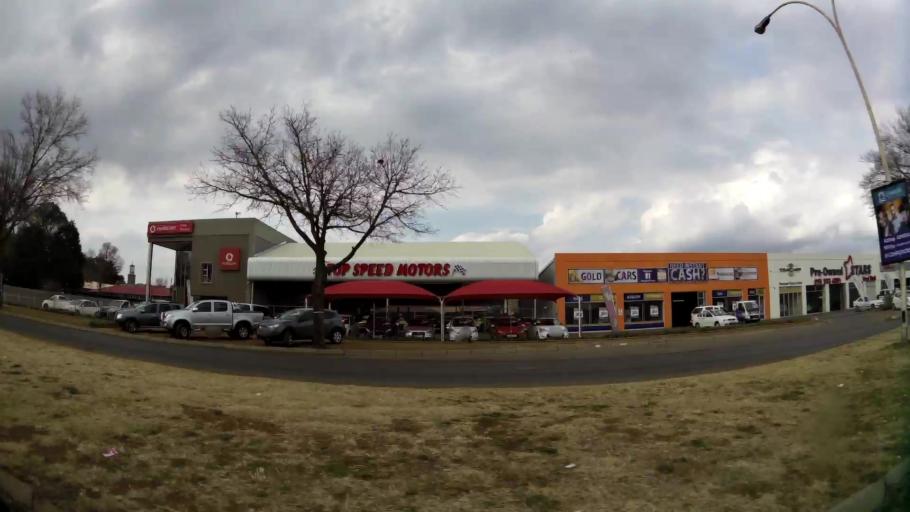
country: ZA
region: Gauteng
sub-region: Sedibeng District Municipality
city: Vanderbijlpark
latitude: -26.7090
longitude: 27.8248
